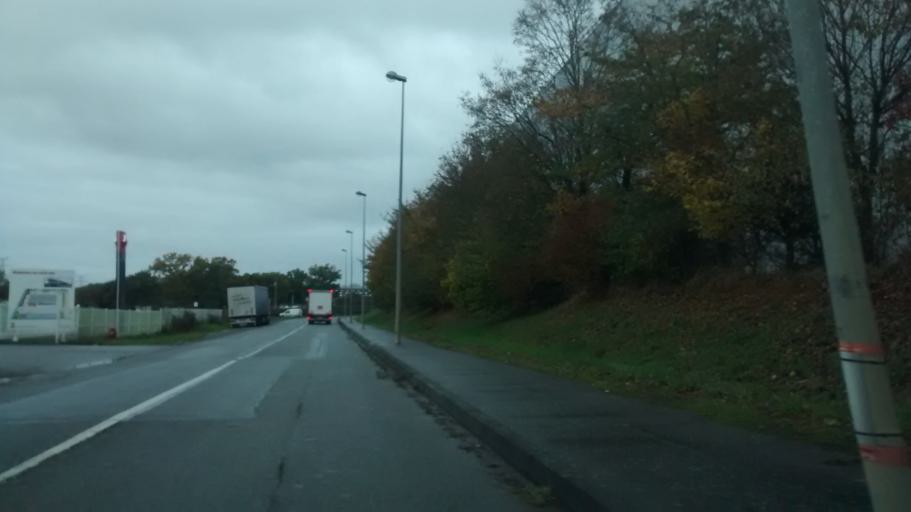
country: FR
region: Brittany
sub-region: Departement d'Ille-et-Vilaine
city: Noyal-sur-Vilaine
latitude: 48.1040
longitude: -1.5086
